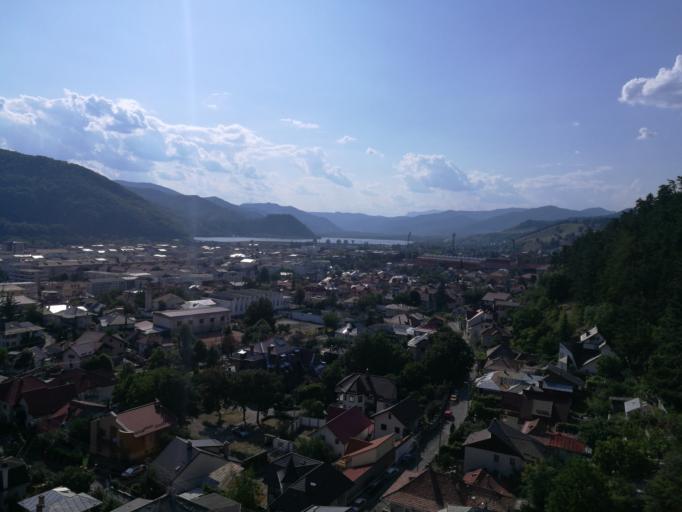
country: RO
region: Neamt
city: Piatra Neamt
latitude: 46.9376
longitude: 26.3647
